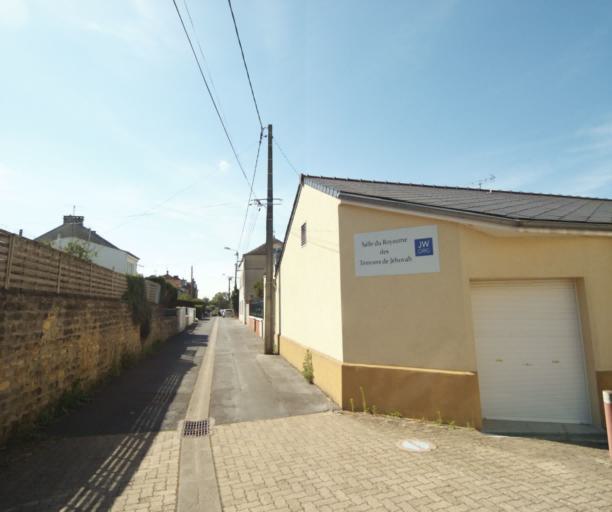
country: FR
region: Champagne-Ardenne
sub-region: Departement des Ardennes
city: Charleville-Mezieres
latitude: 49.7620
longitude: 4.7086
